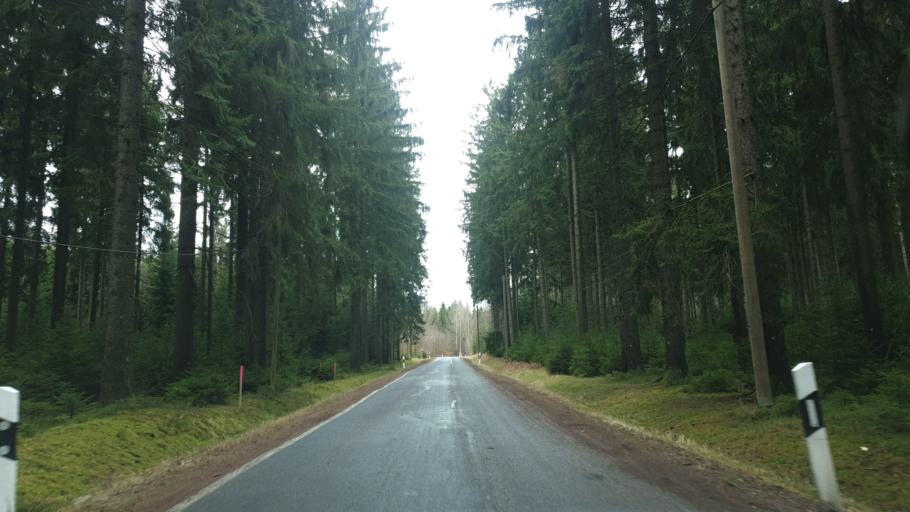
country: CZ
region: Karlovarsky
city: Hranice
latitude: 50.2942
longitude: 12.2004
